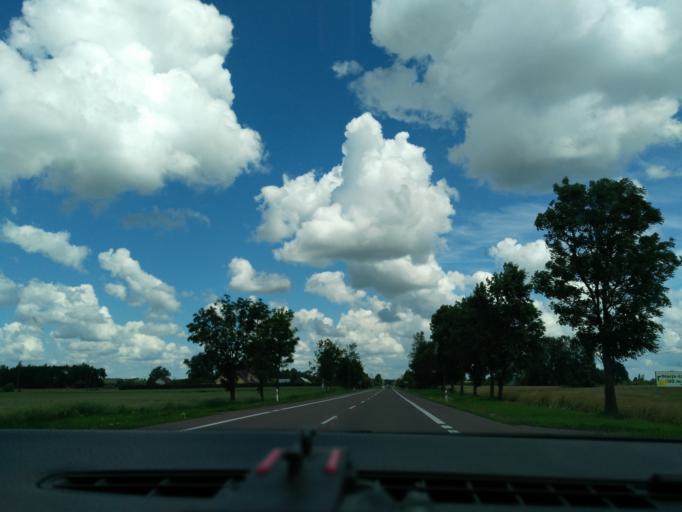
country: PL
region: Podlasie
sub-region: Powiat bielski
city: Bielsk Podlaski
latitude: 52.7974
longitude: 23.1913
